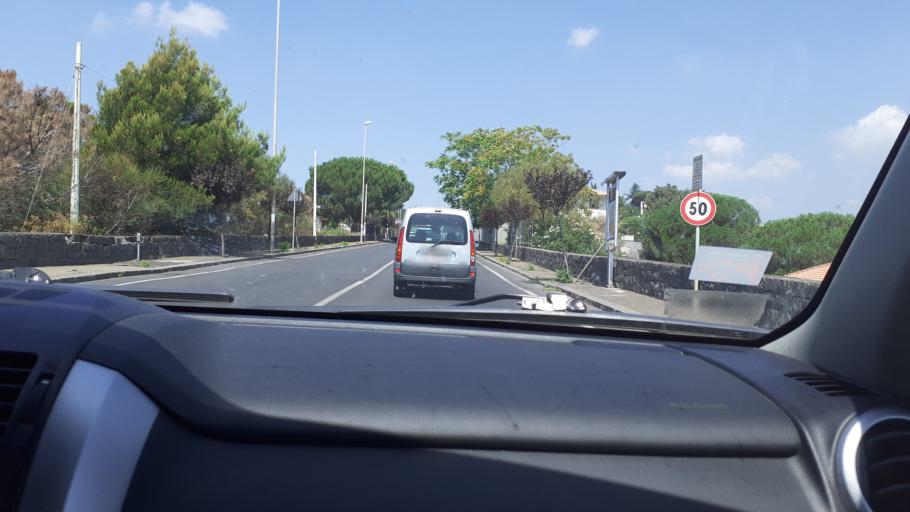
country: IT
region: Sicily
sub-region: Catania
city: Nicolosi
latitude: 37.6151
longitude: 15.0355
